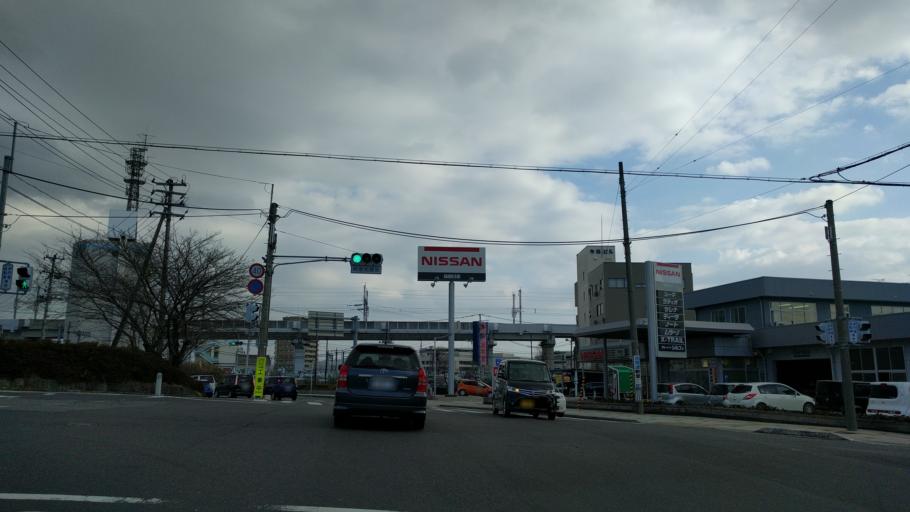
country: JP
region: Fukushima
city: Koriyama
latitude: 37.4043
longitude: 140.3879
